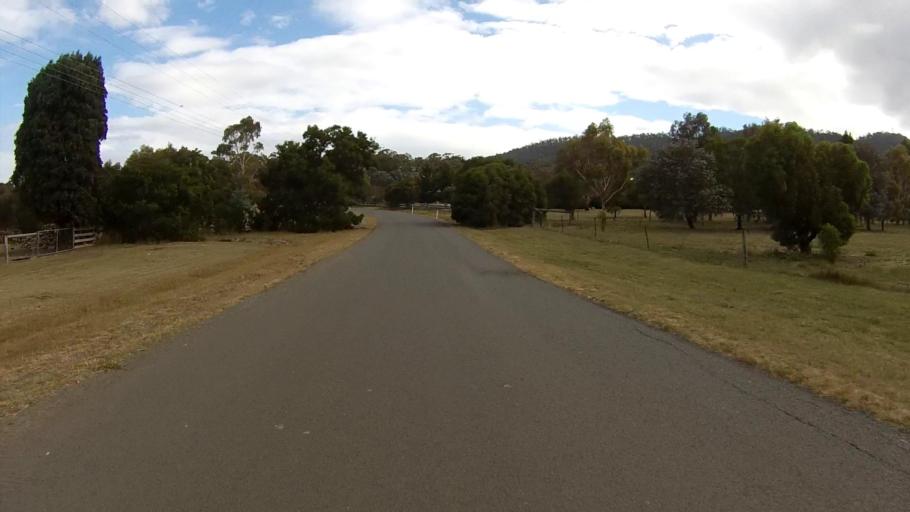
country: AU
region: Tasmania
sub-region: Clarence
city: Seven Mile Beach
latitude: -42.8565
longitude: 147.4832
